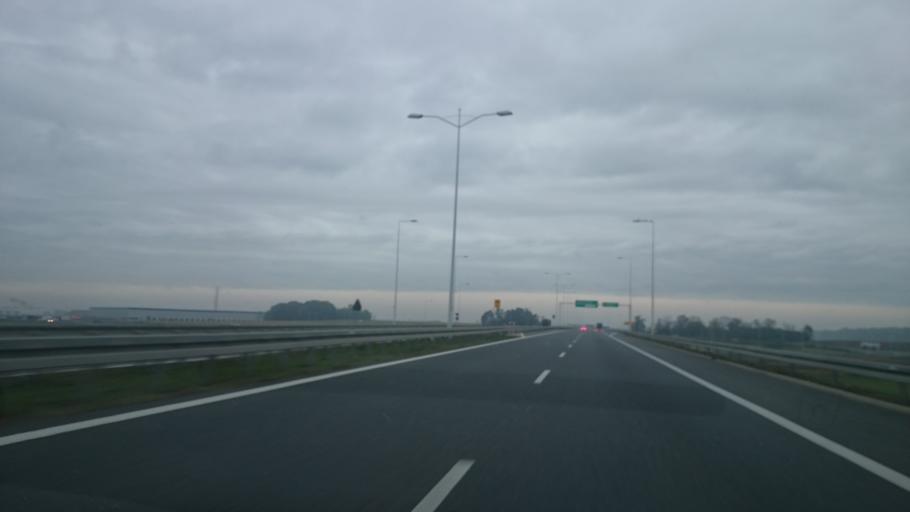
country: PL
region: Lower Silesian Voivodeship
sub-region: Powiat wroclawski
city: Tyniec Maly
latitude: 51.0274
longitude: 16.9403
